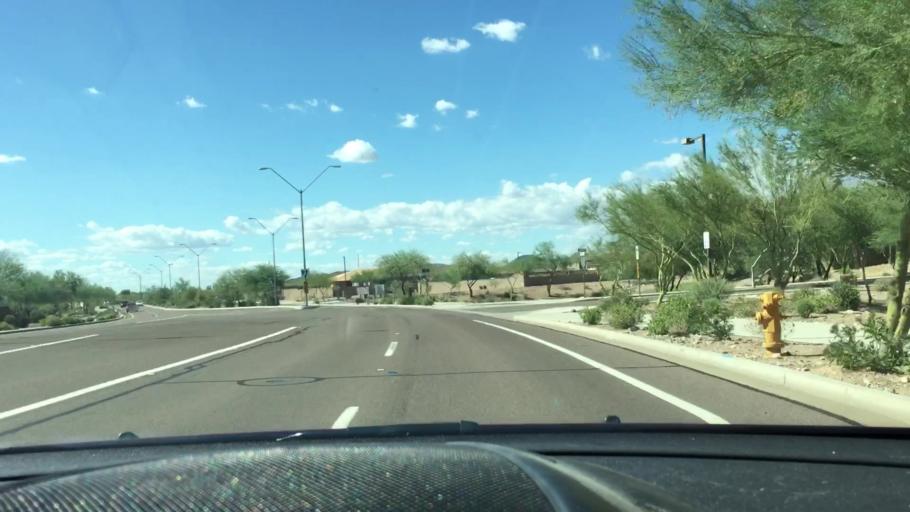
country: US
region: Arizona
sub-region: Maricopa County
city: Sun City West
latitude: 33.7370
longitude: -112.2559
